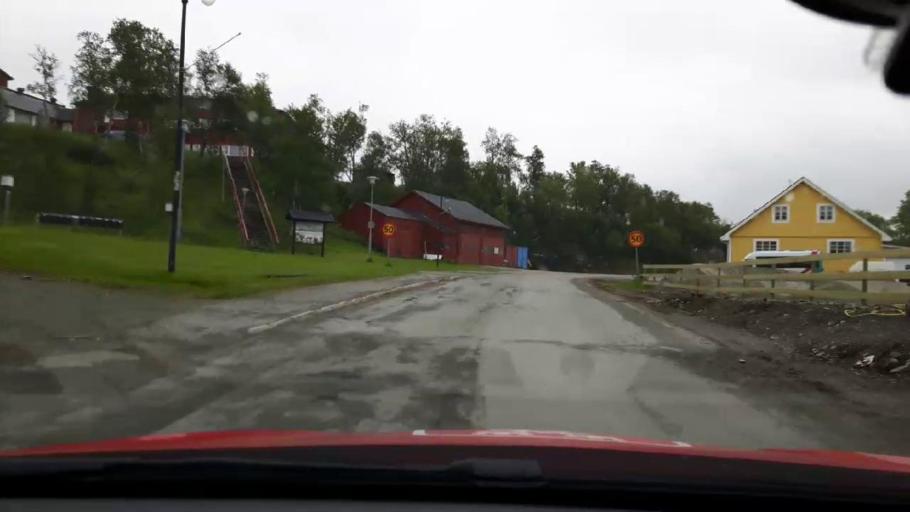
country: NO
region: Nord-Trondelag
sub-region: Meraker
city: Meraker
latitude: 63.3154
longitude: 12.1043
